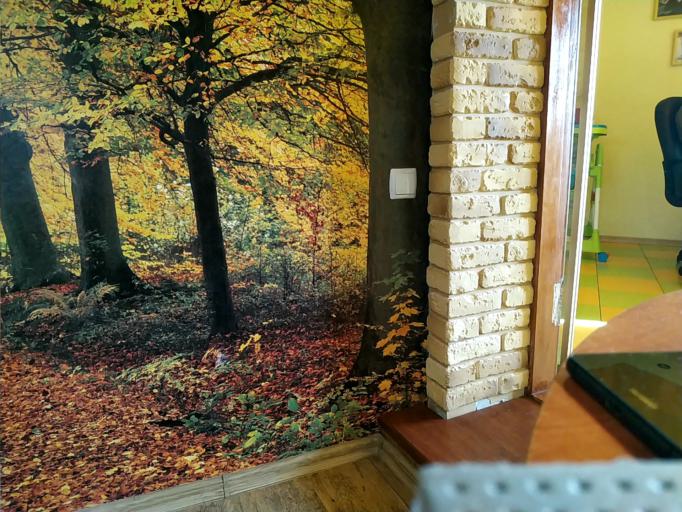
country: RU
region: Tverskaya
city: Zubtsov
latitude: 56.2042
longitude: 34.5965
